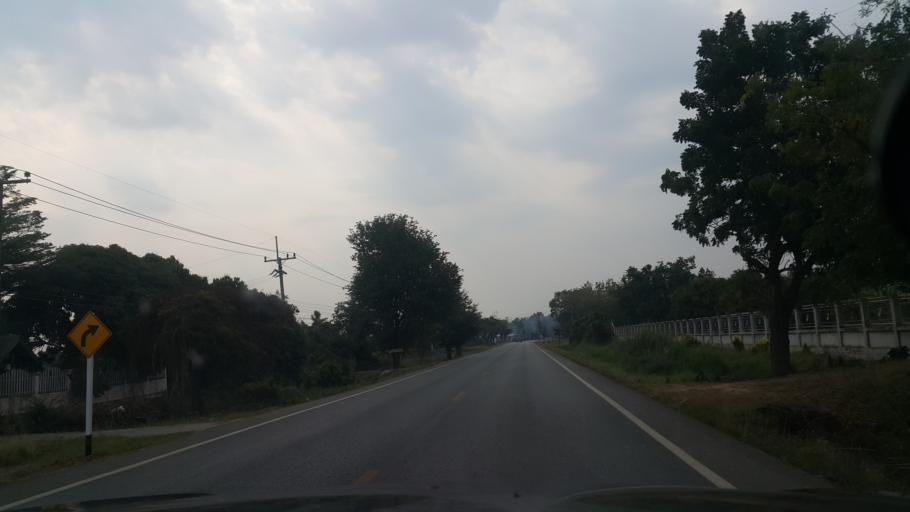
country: TH
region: Sukhothai
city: Si Samrong
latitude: 17.1098
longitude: 99.8892
